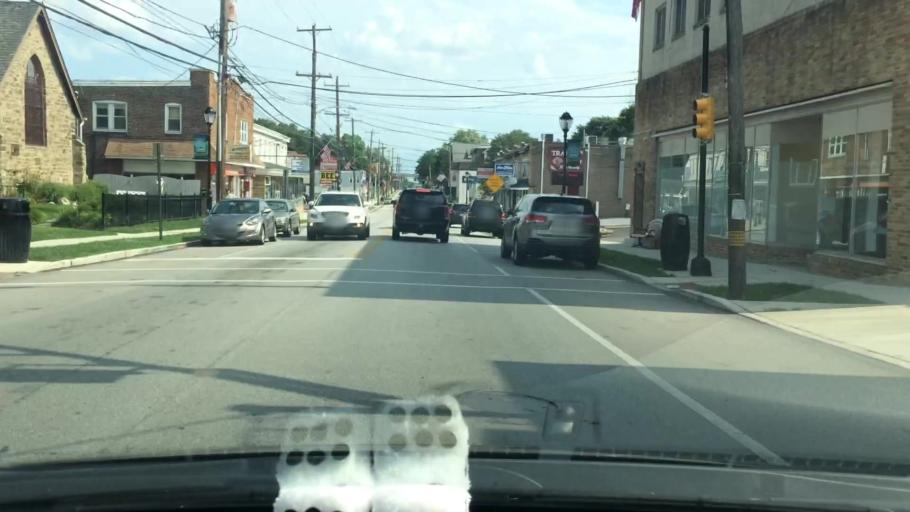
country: US
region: Pennsylvania
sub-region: Delaware County
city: Prospect Park
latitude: 39.8869
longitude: -75.3095
